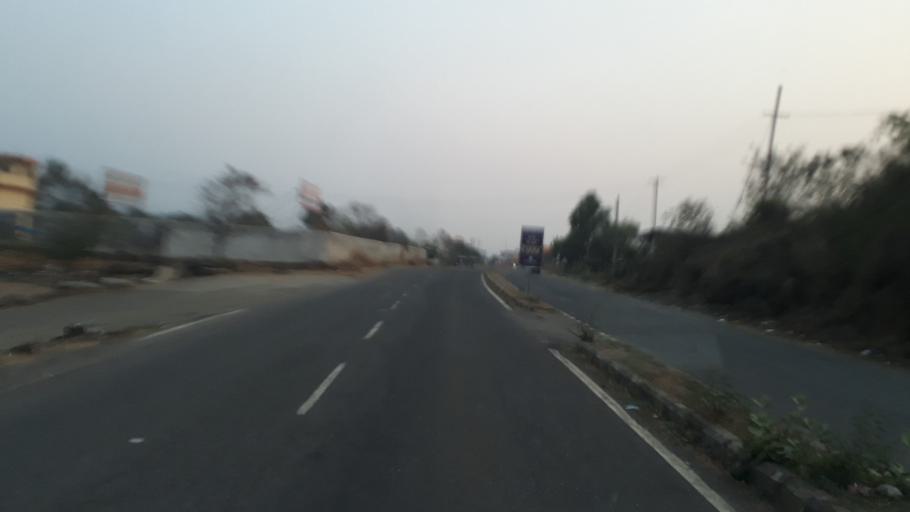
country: IN
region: Maharashtra
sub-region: Raigarh
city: Neral
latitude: 18.9726
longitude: 73.3292
